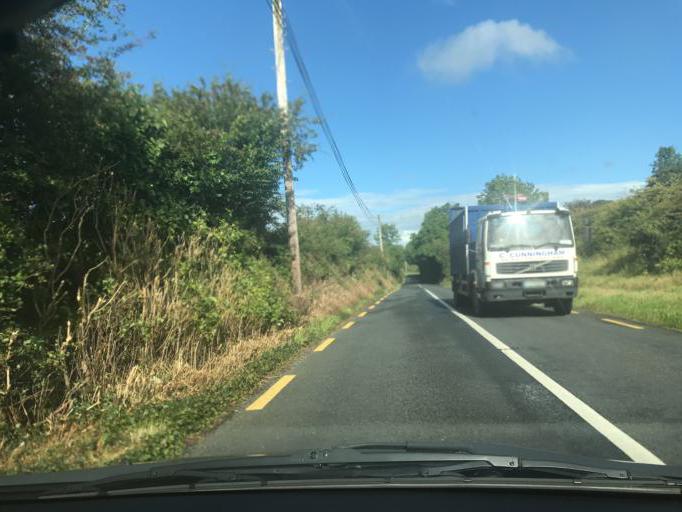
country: IE
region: Connaught
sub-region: Sligo
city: Collooney
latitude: 54.1849
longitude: -8.4676
